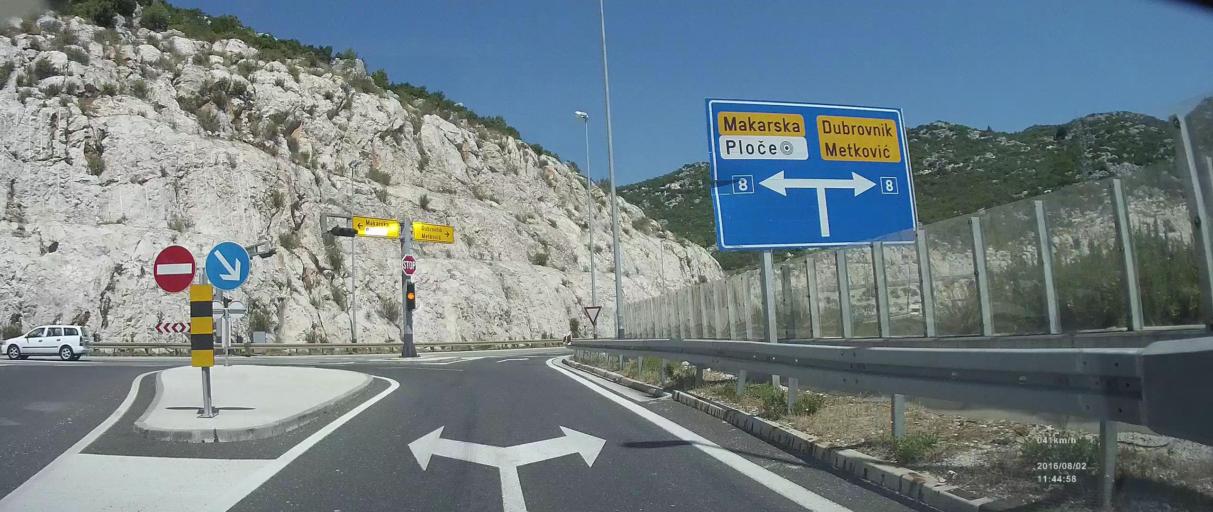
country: HR
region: Dubrovacko-Neretvanska
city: Komin
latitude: 43.0529
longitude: 17.4618
